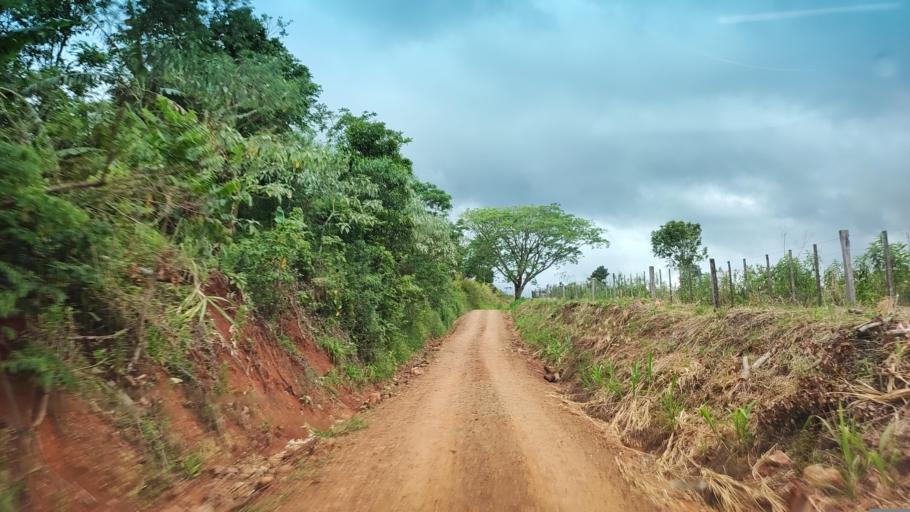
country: AR
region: Misiones
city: Dos de Mayo
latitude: -27.0087
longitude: -54.6218
